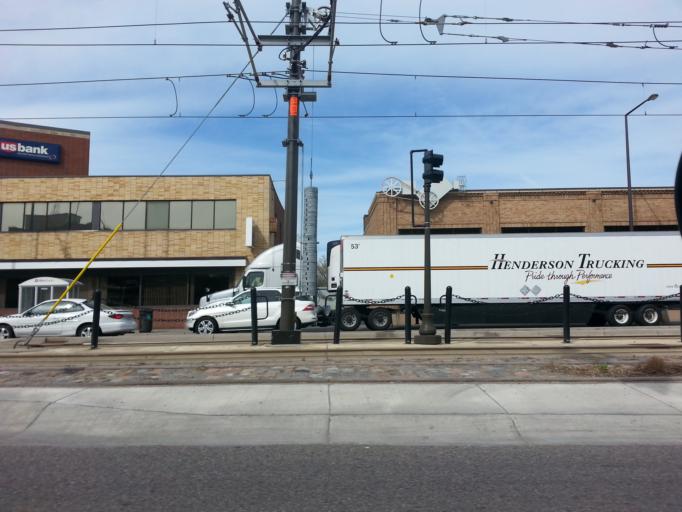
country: US
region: Minnesota
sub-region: Ramsey County
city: Lauderdale
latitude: 44.9638
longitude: -93.1974
